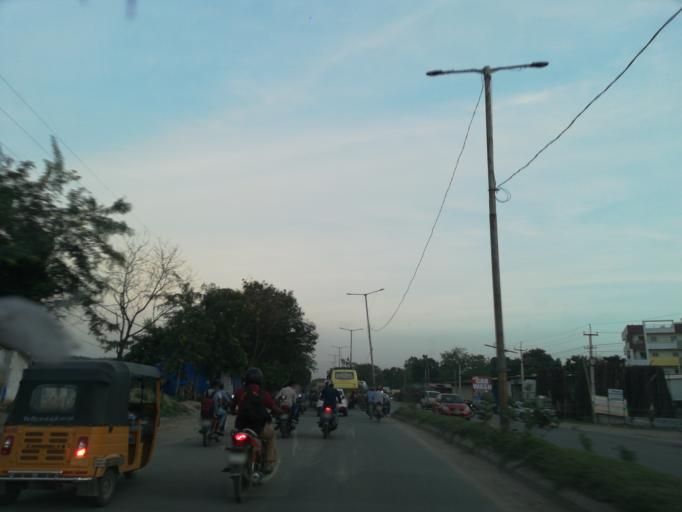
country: IN
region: Telangana
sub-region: Medak
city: Serilingampalle
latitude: 17.5185
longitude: 78.3563
